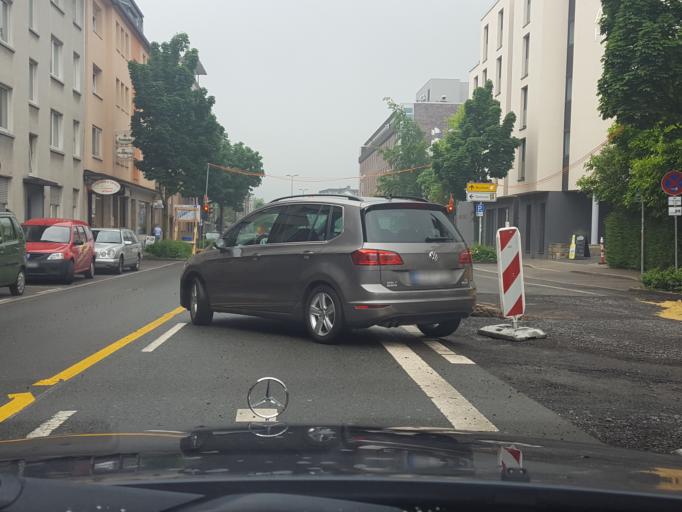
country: DE
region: North Rhine-Westphalia
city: Witten
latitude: 51.4438
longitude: 7.3384
